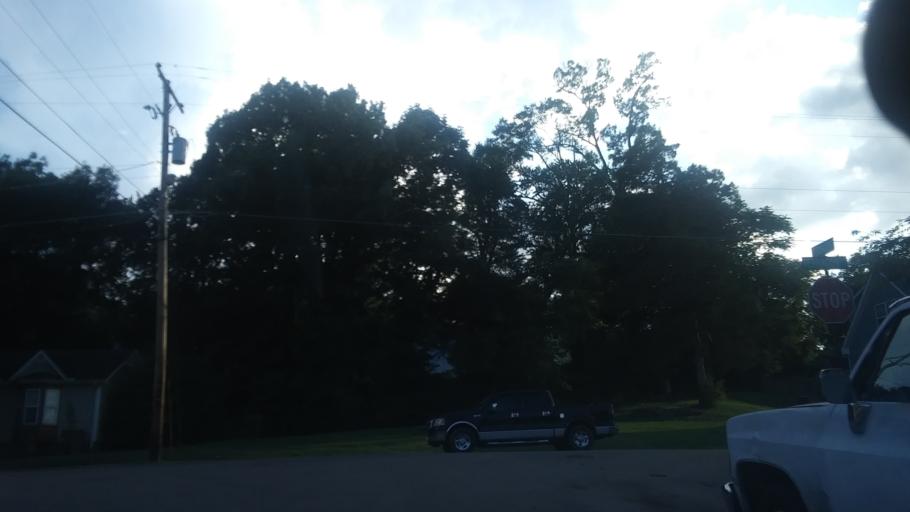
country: US
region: Tennessee
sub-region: Rutherford County
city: La Vergne
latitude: 36.0756
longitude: -86.6706
